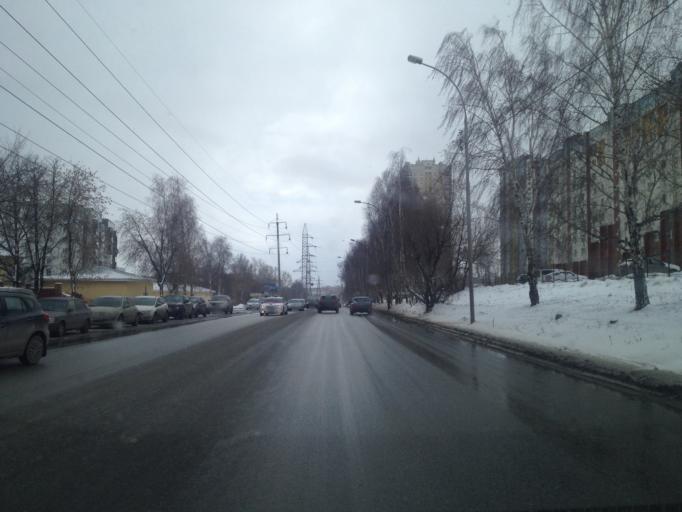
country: RU
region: Sverdlovsk
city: Sovkhoznyy
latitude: 56.7802
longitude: 60.5984
